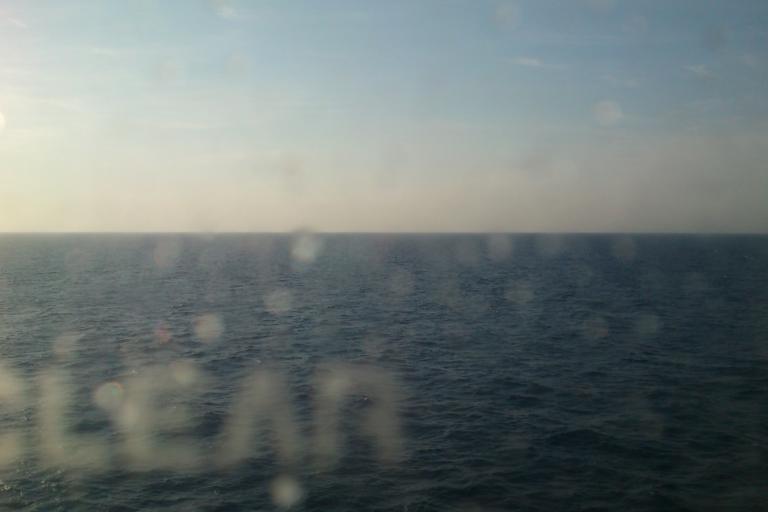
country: JP
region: Ishikawa
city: Nanao
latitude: 37.8075
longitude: 136.4436
